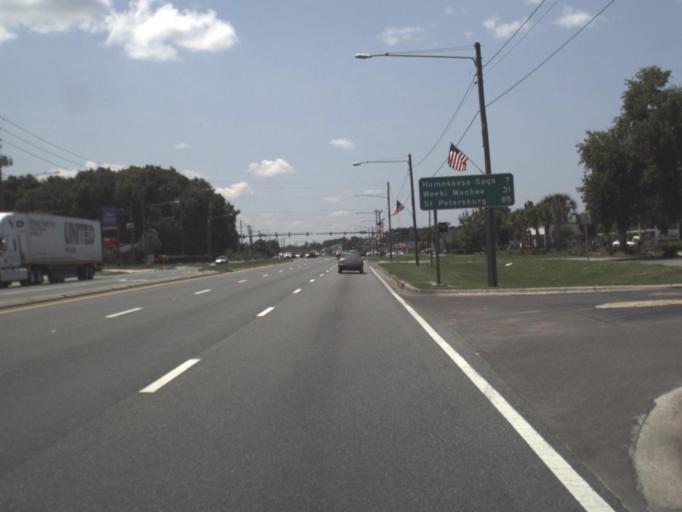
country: US
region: Florida
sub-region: Citrus County
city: Crystal River
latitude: 28.8944
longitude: -82.5848
